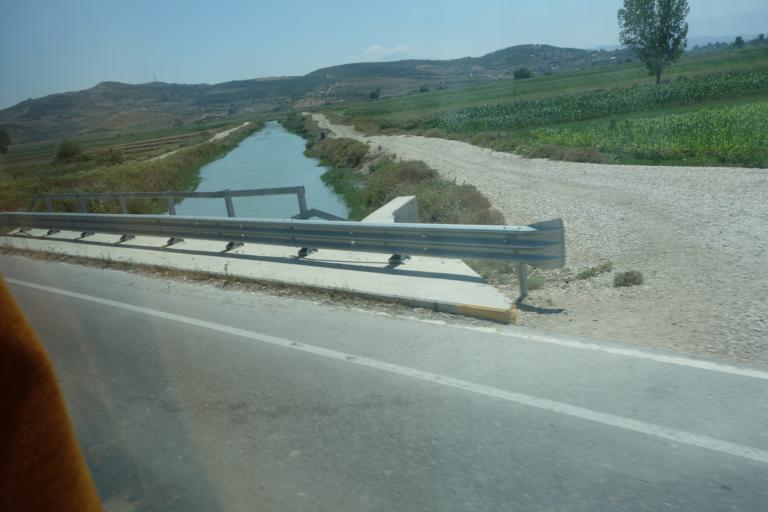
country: AL
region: Fier
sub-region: Rrethi i Fierit
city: Cakran
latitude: 40.5942
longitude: 19.5761
